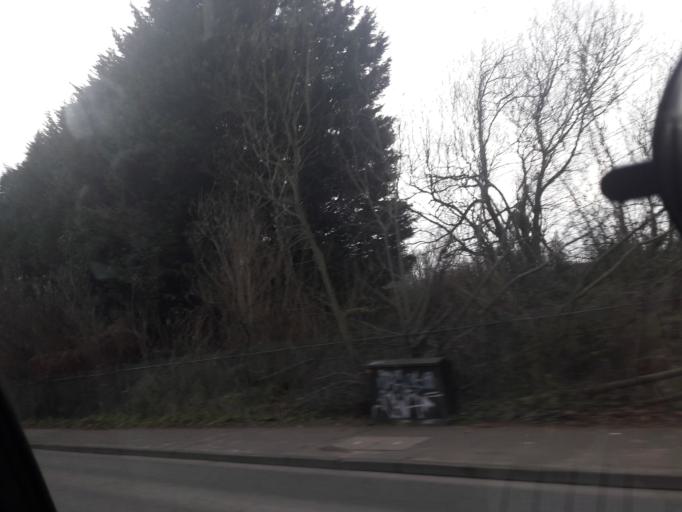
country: GB
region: Northern Ireland
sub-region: City of Belfast
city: Belfast
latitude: 54.6236
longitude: -5.9497
